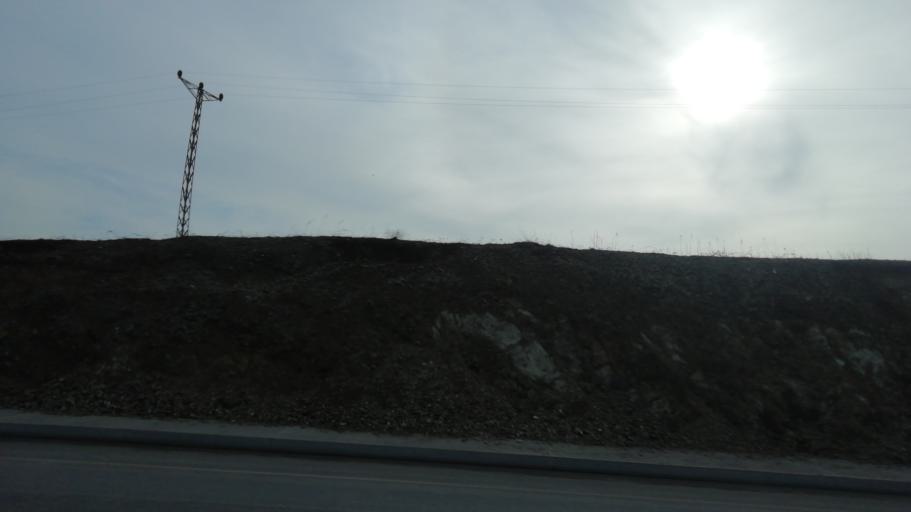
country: TR
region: Istanbul
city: Basaksehir
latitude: 41.1296
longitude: 28.7876
